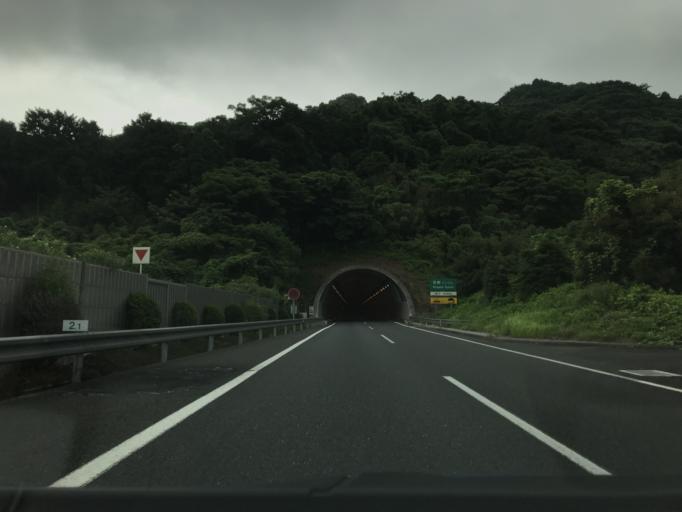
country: JP
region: Fukuoka
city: Kitakyushu
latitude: 33.8137
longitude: 130.9066
